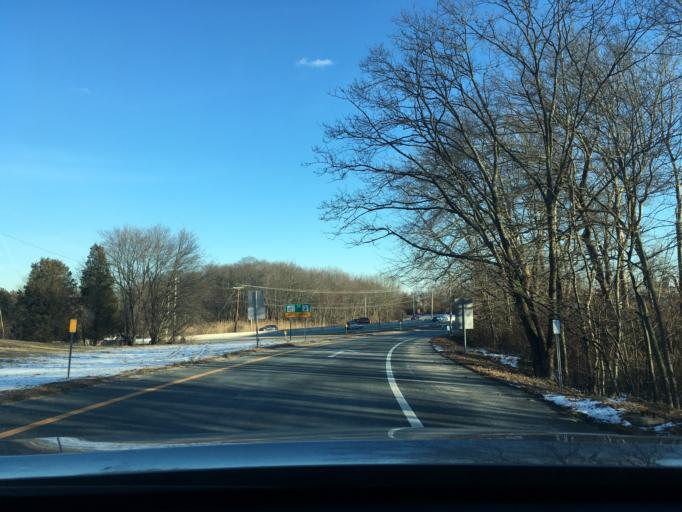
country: US
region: Rhode Island
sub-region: Kent County
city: West Warwick
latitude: 41.6663
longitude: -71.5010
